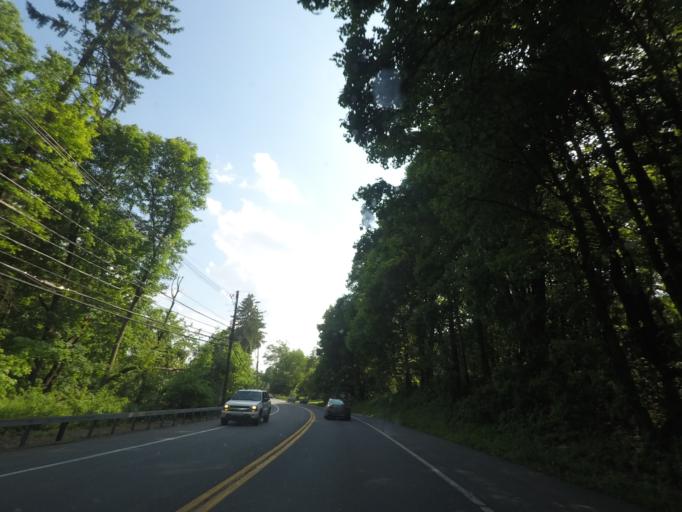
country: US
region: New York
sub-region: Orange County
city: Balmville
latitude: 41.5642
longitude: -74.0009
